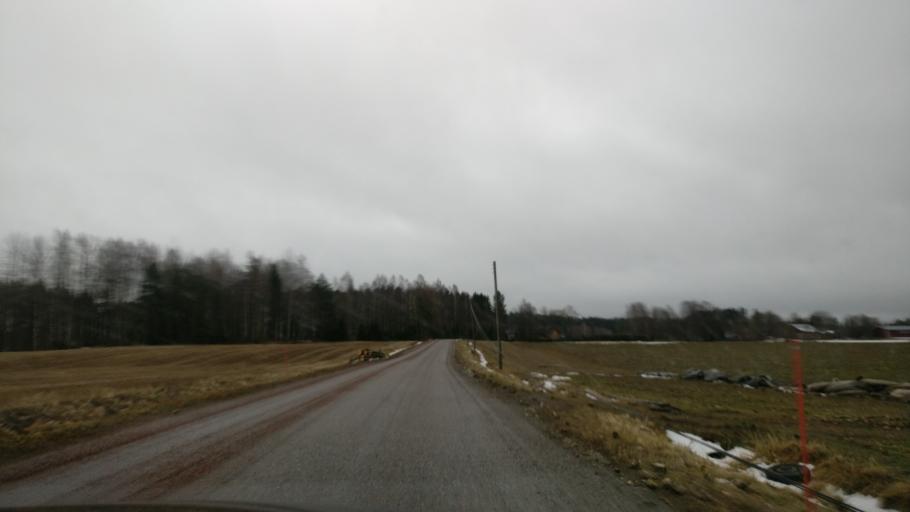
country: FI
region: Uusimaa
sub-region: Raaseporin
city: Karis
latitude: 60.0928
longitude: 23.7750
